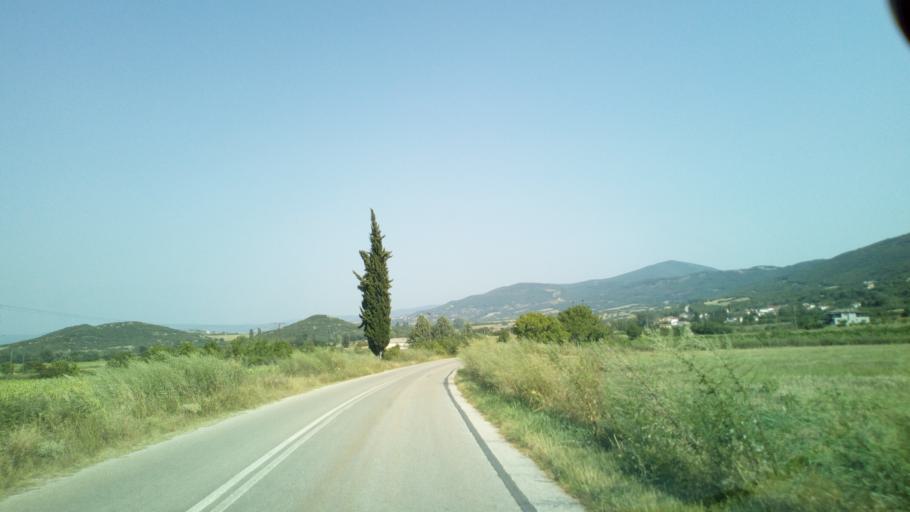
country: GR
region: Central Macedonia
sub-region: Nomos Chalkidikis
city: Galatista
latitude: 40.5120
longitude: 23.3666
